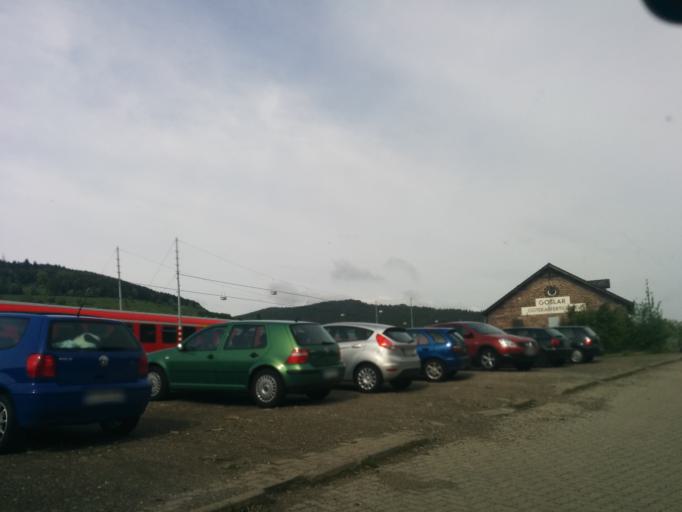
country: DE
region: Lower Saxony
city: Goslar
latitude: 51.9120
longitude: 10.4223
